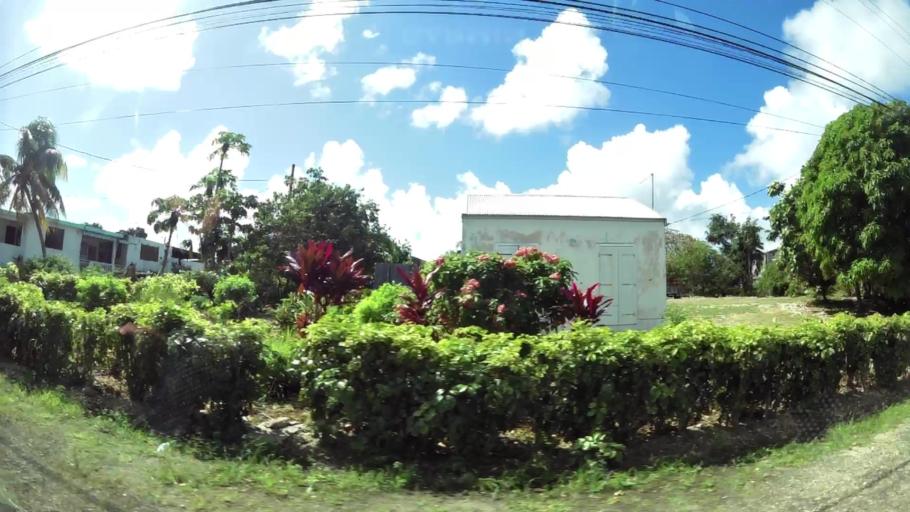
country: GP
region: Guadeloupe
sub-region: Guadeloupe
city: Anse-Bertrand
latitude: 16.4567
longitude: -61.4799
